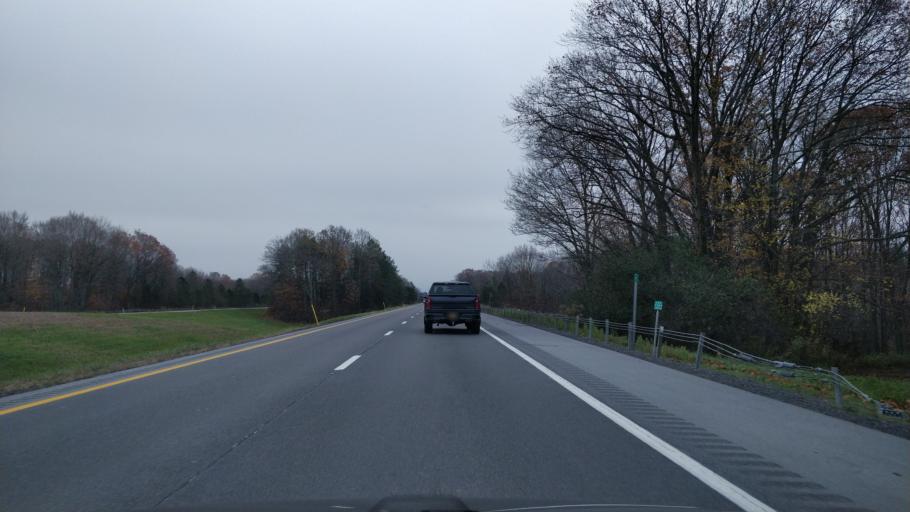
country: US
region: New York
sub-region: Jefferson County
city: Adams
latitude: 43.7010
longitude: -76.0752
